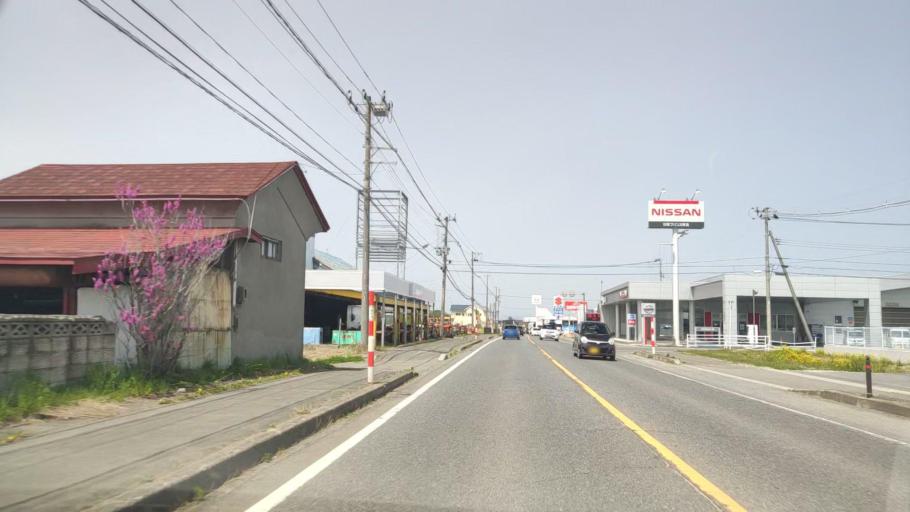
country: JP
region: Aomori
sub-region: Misawa Shi
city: Inuotose
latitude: 40.6490
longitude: 141.1966
